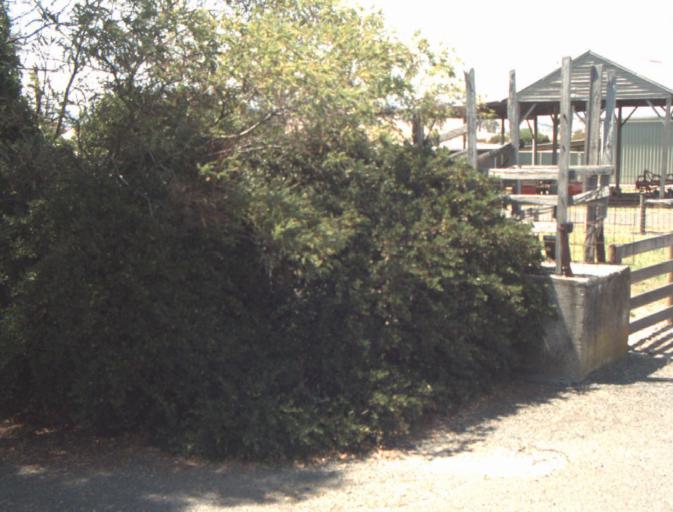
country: AU
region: Tasmania
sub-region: Northern Midlands
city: Perth
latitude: -41.5079
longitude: 147.2078
